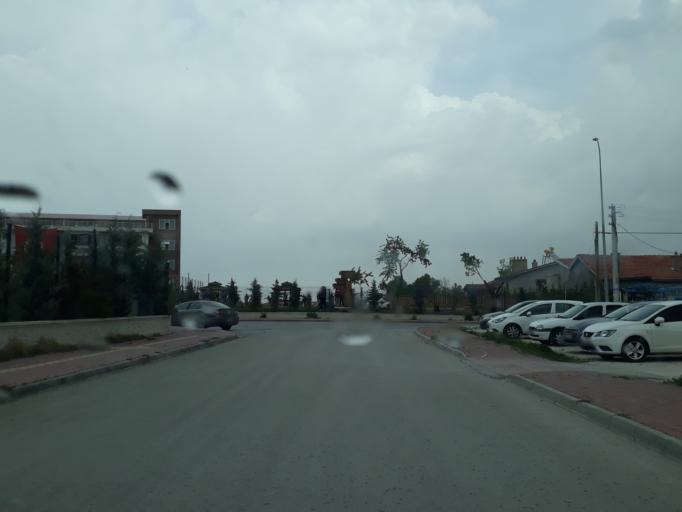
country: TR
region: Konya
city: Sille
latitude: 37.9199
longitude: 32.4620
